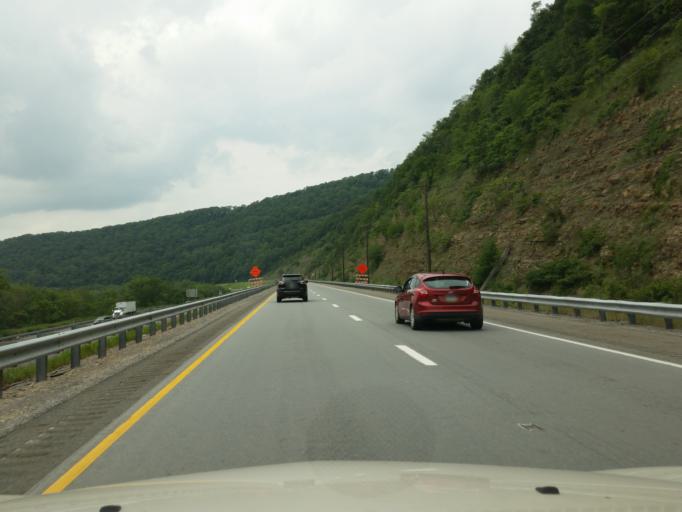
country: US
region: Pennsylvania
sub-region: Perry County
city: Newport
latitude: 40.5599
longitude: -77.1645
